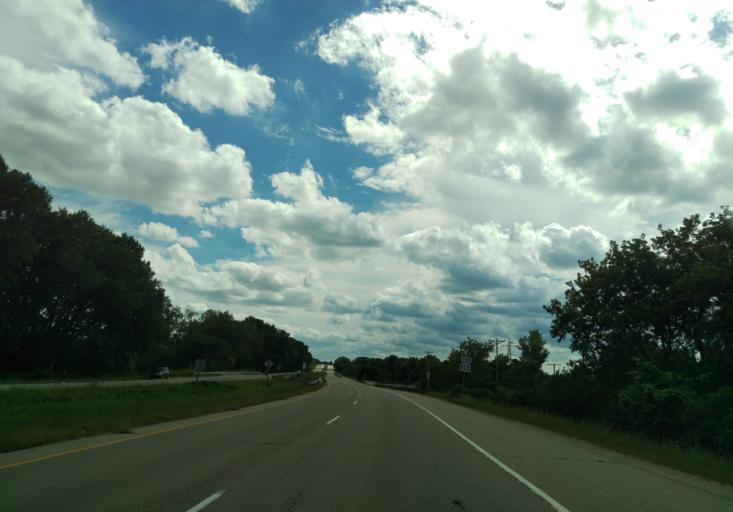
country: US
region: Wisconsin
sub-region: Dane County
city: Maple Bluff
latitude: 43.1519
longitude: -89.4032
